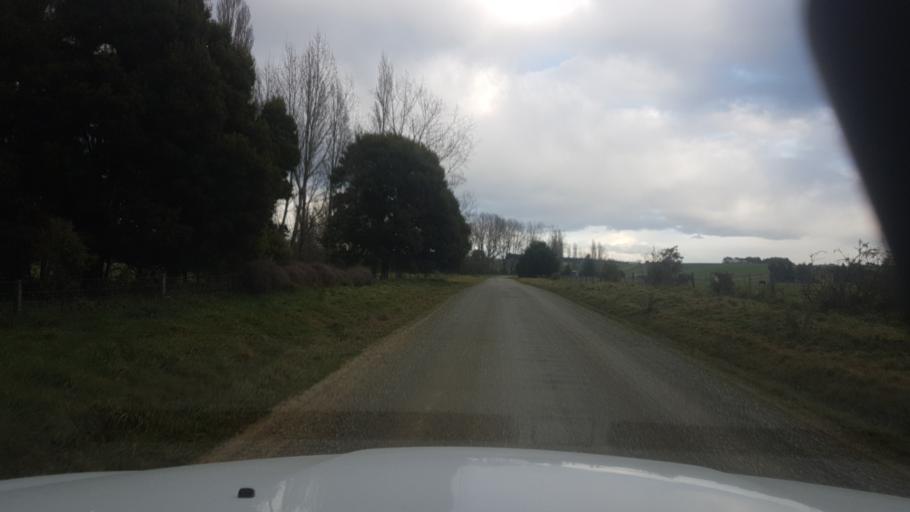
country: NZ
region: Canterbury
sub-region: Timaru District
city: Timaru
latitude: -44.3391
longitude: 171.1915
